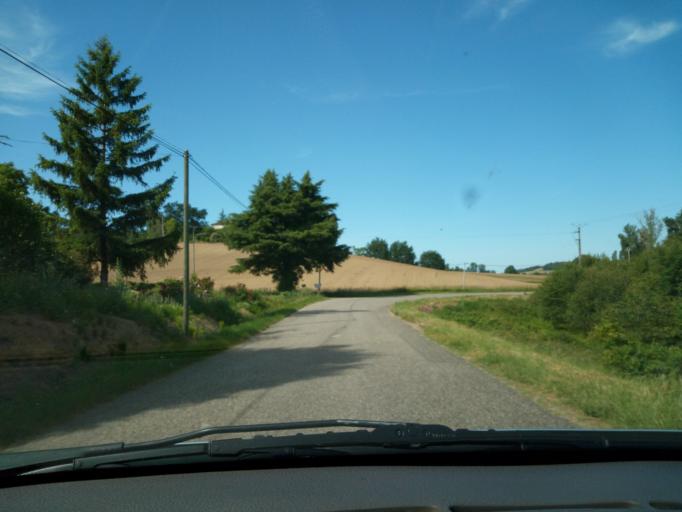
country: FR
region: Midi-Pyrenees
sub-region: Departement du Tarn-et-Garonne
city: Molieres
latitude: 44.2126
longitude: 1.3133
